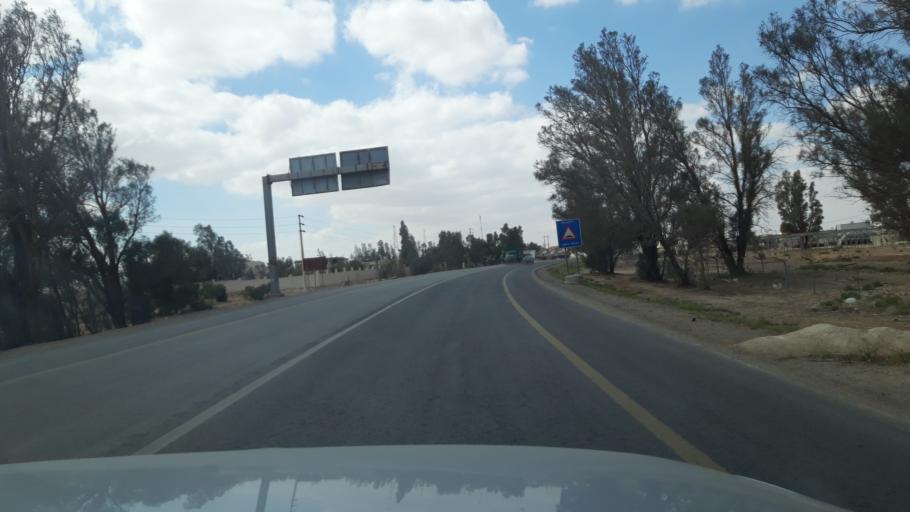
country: JO
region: Amman
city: Al Azraq ash Shamali
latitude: 31.8376
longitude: 36.8127
